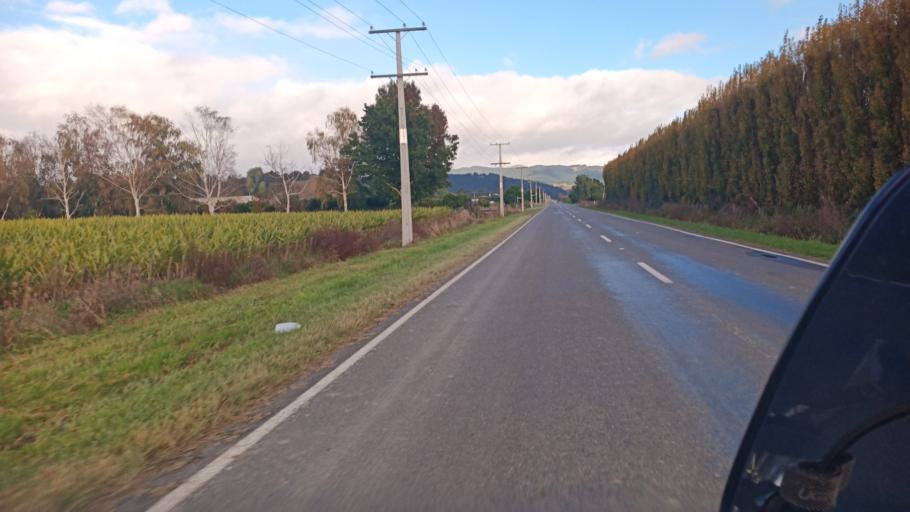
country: NZ
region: Gisborne
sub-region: Gisborne District
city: Gisborne
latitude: -38.6314
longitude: 177.8857
